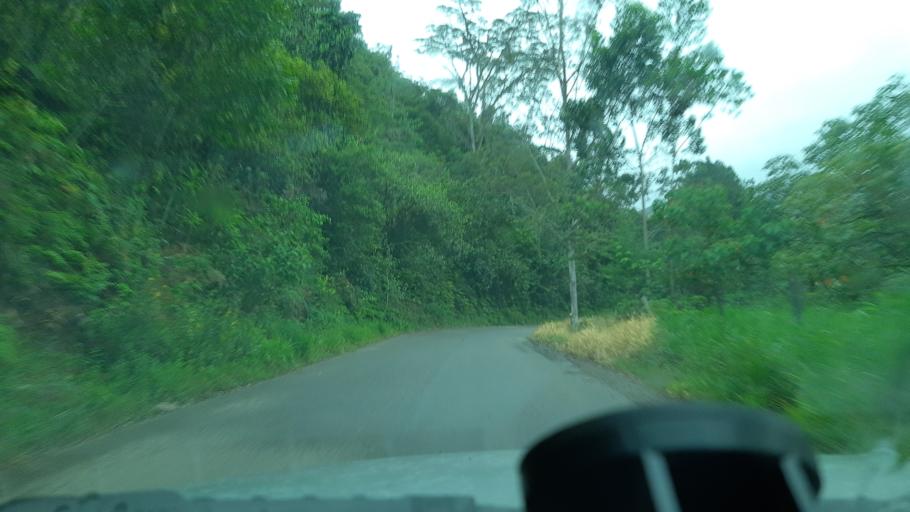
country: CO
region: Boyaca
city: Chinavita
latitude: 5.1943
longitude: -73.3819
